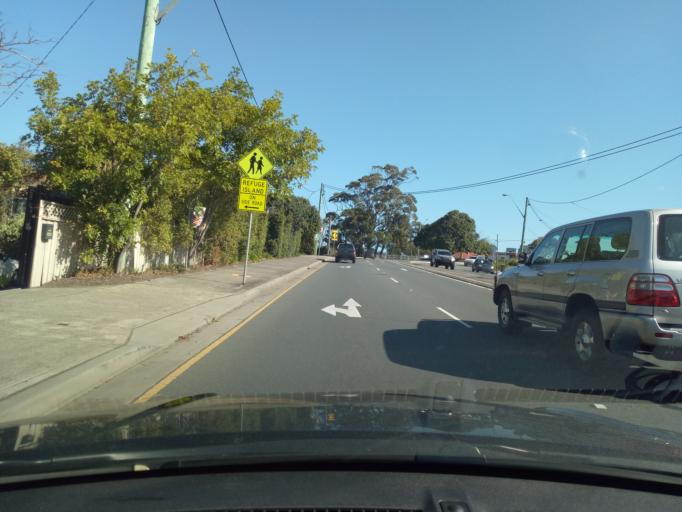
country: AU
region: New South Wales
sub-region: Gosford Shire
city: Holgate
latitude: -33.4217
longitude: 151.4392
